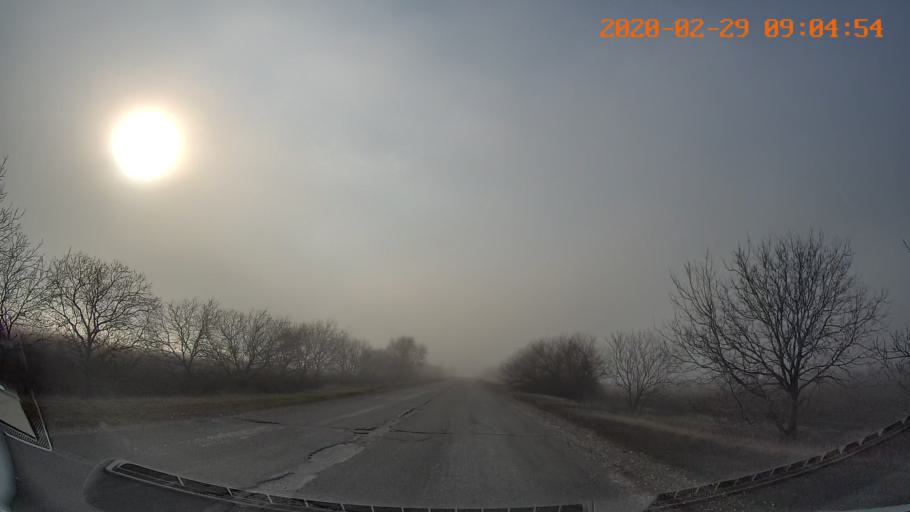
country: MD
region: Telenesti
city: Tiraspolul Nou
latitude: 46.8960
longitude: 29.7381
